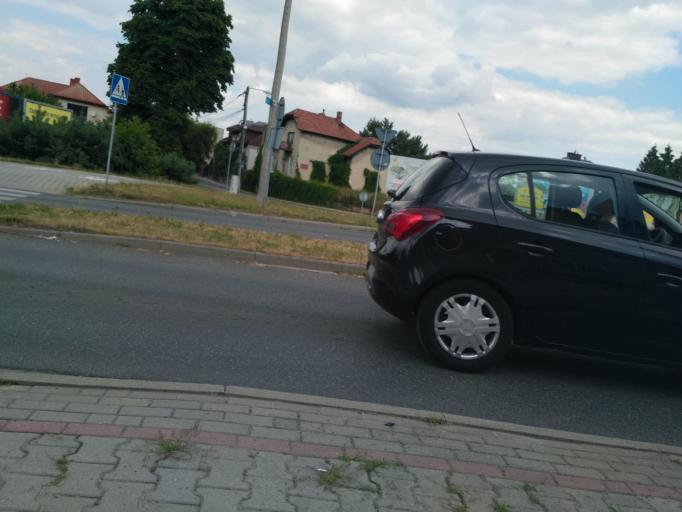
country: PL
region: Subcarpathian Voivodeship
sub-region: Powiat debicki
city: Debica
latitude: 50.0492
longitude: 21.4167
